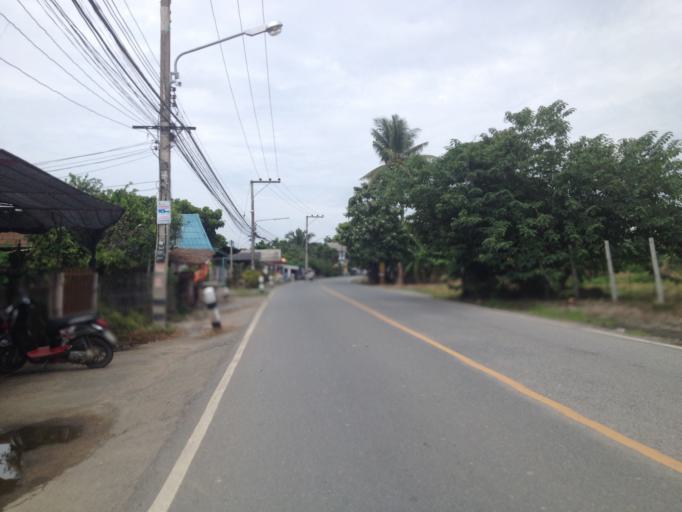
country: TH
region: Chiang Mai
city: Saraphi
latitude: 18.7117
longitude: 98.9829
